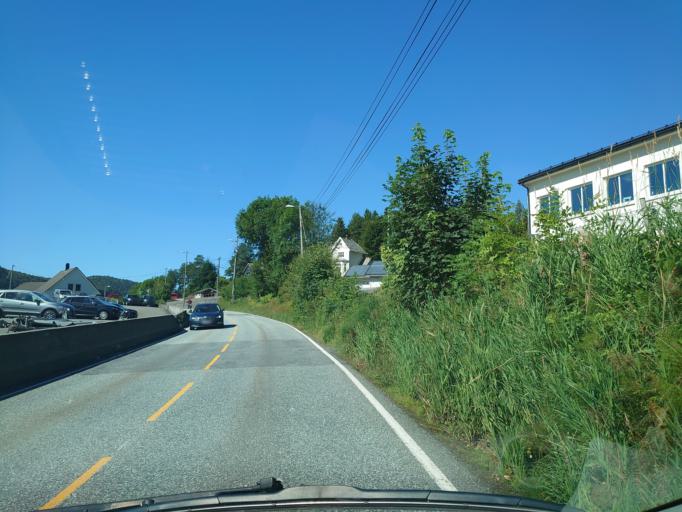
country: NO
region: Hordaland
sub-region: Bergen
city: Indre Arna
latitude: 60.4304
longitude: 5.4677
